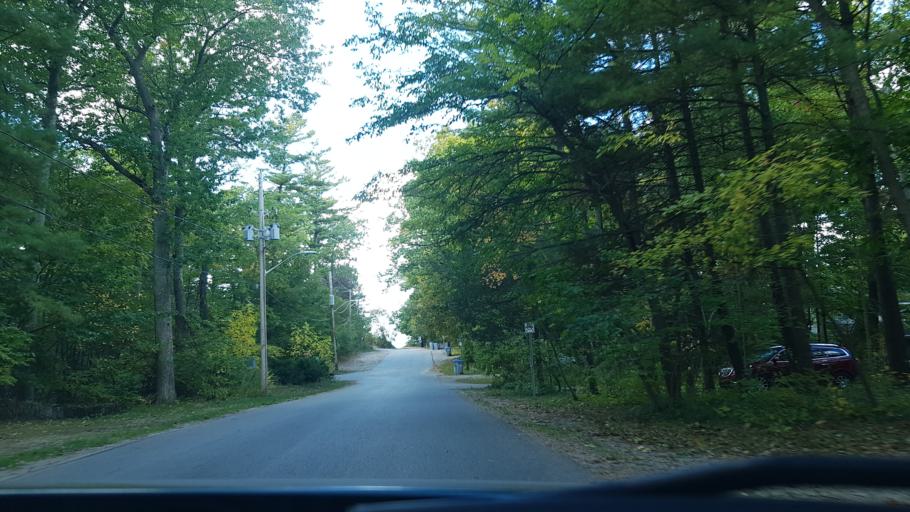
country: CA
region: Ontario
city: Lambton Shores
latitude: 43.3116
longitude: -81.7657
